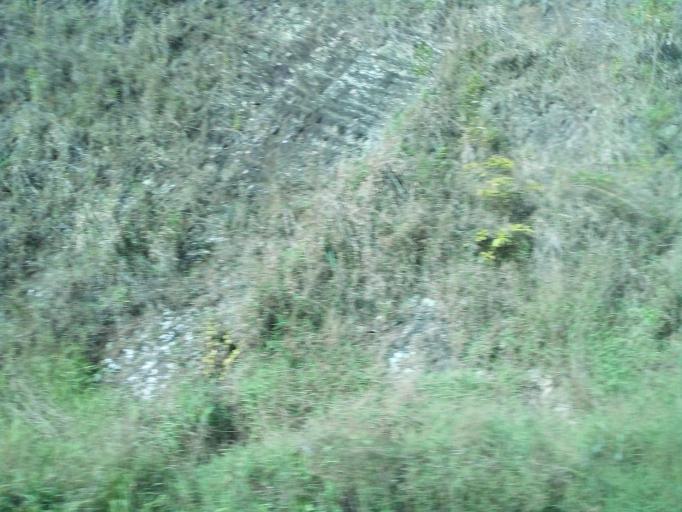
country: BR
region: Minas Gerais
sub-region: Caete
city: Caete
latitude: -19.8741
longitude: -43.7673
